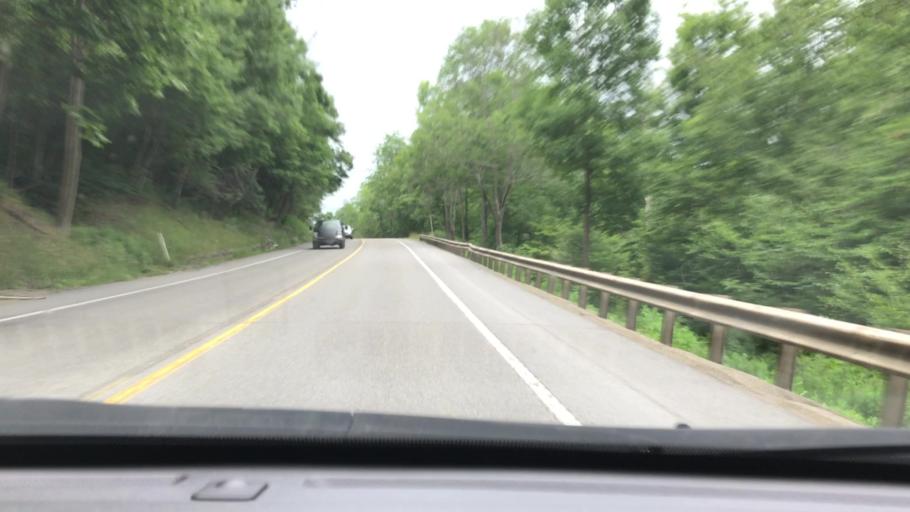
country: US
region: Pennsylvania
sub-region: McKean County
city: Bradford
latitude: 41.8537
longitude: -78.6756
